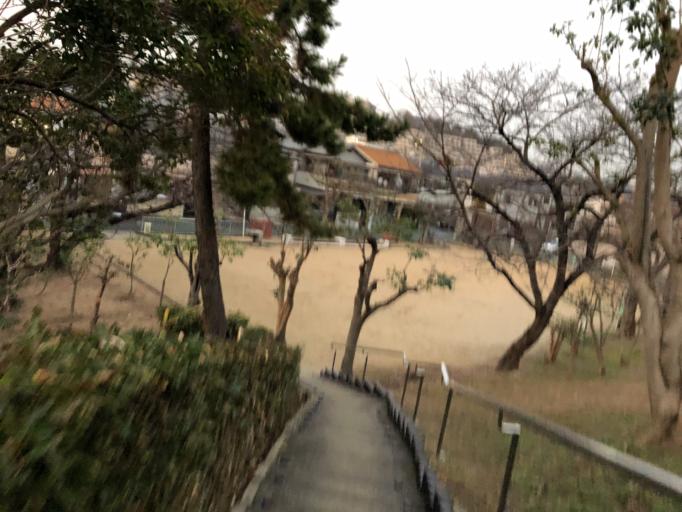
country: JP
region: Hyogo
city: Akashi
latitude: 34.6536
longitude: 135.0201
